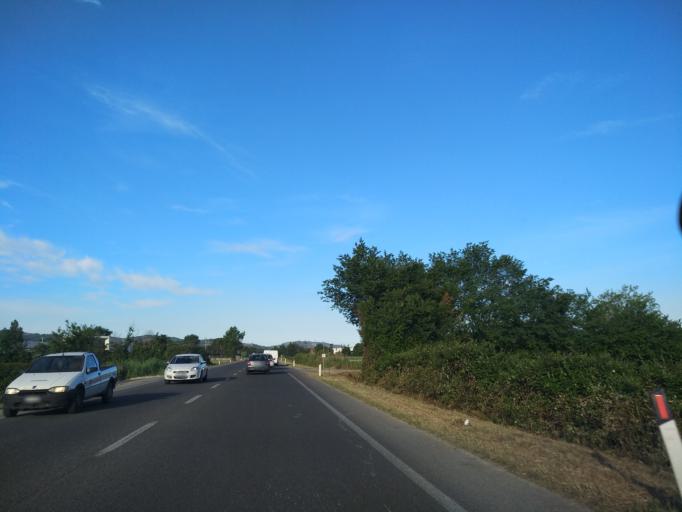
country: IT
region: The Marches
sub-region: Provincia di Pesaro e Urbino
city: Villa Ceccolini
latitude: 43.8774
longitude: 12.8473
